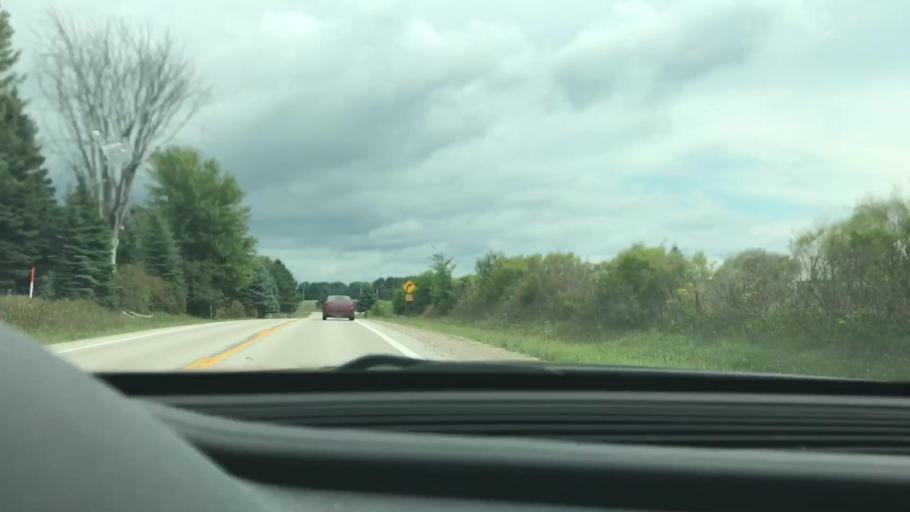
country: US
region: Michigan
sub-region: Antrim County
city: Bellaire
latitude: 45.0943
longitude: -85.2939
